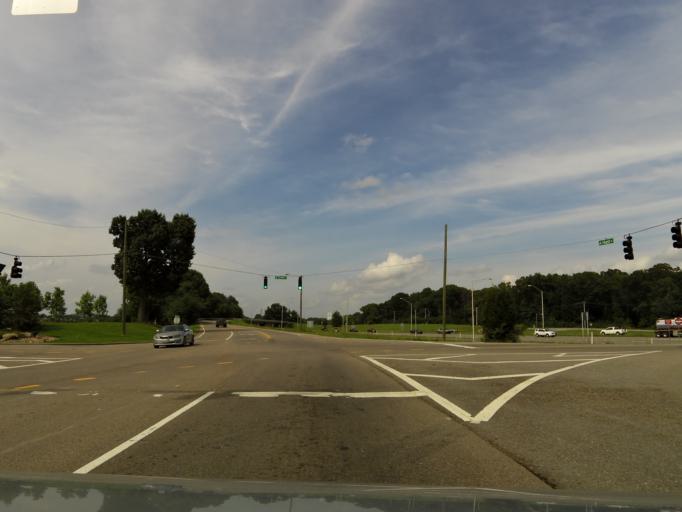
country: US
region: Tennessee
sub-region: Blount County
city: Alcoa
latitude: 35.7982
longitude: -83.9917
